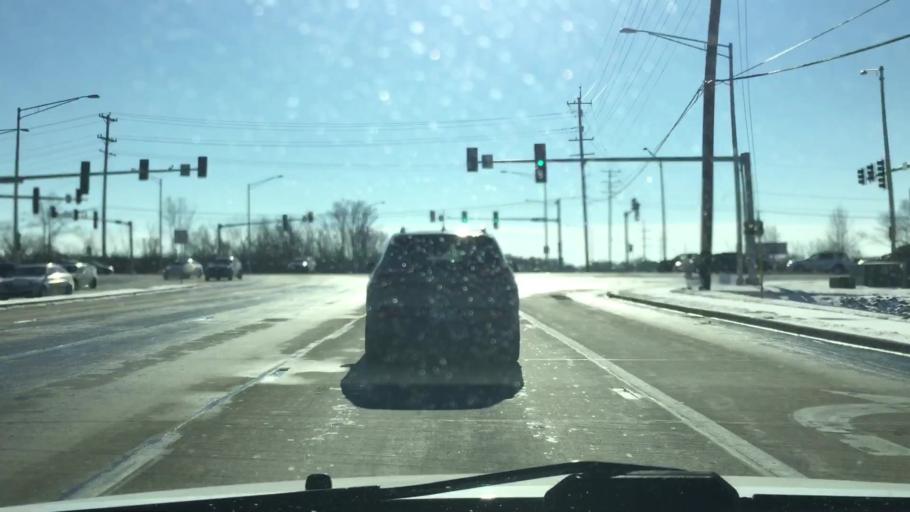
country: US
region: Illinois
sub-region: Kane County
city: Geneva
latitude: 41.8868
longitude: -88.2773
